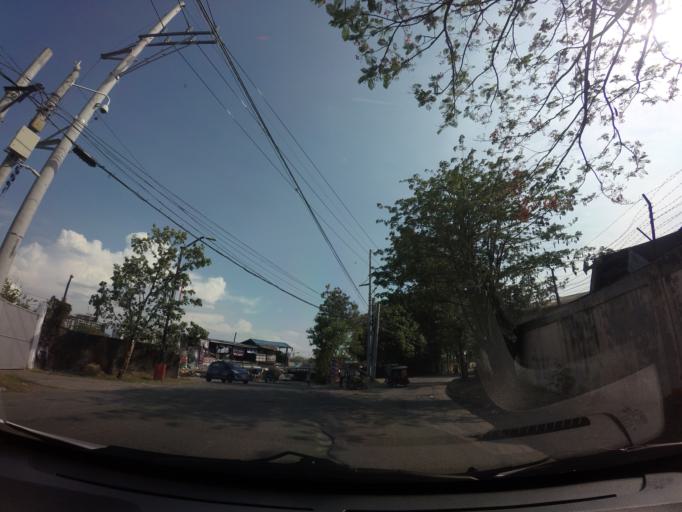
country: PH
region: Calabarzon
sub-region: Province of Rizal
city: Taguig
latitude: 14.5108
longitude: 121.0466
